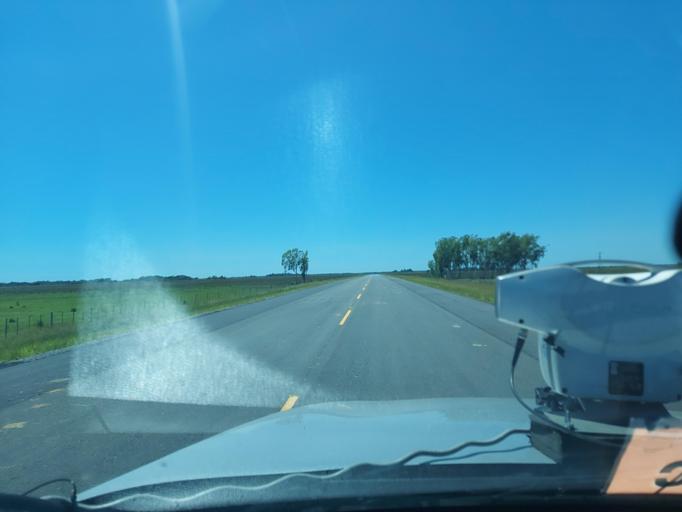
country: PY
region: Neembucu
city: Pilar
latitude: -26.8231
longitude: -58.2471
